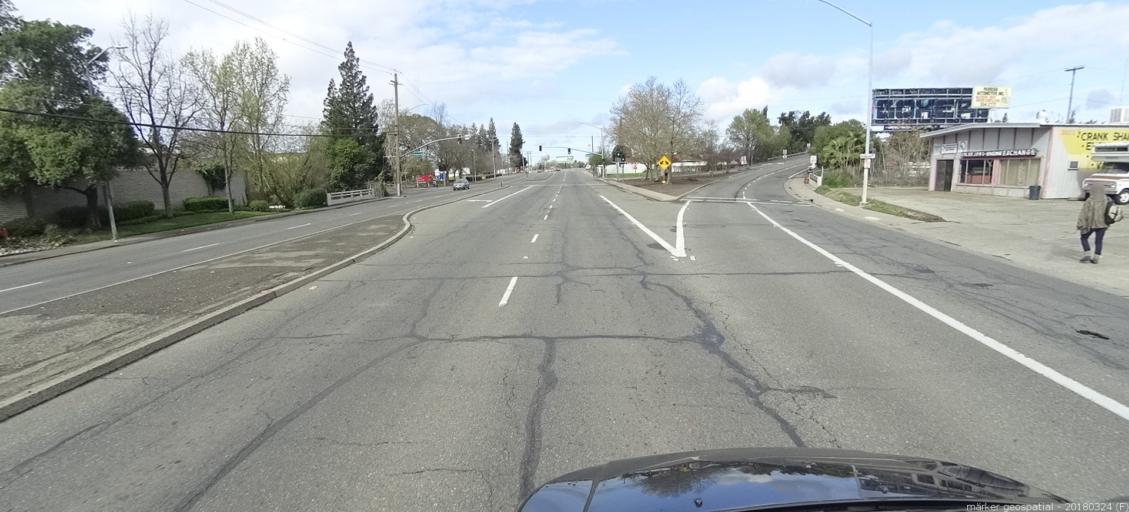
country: US
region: California
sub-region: Sacramento County
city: North Highlands
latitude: 38.6612
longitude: -121.3753
